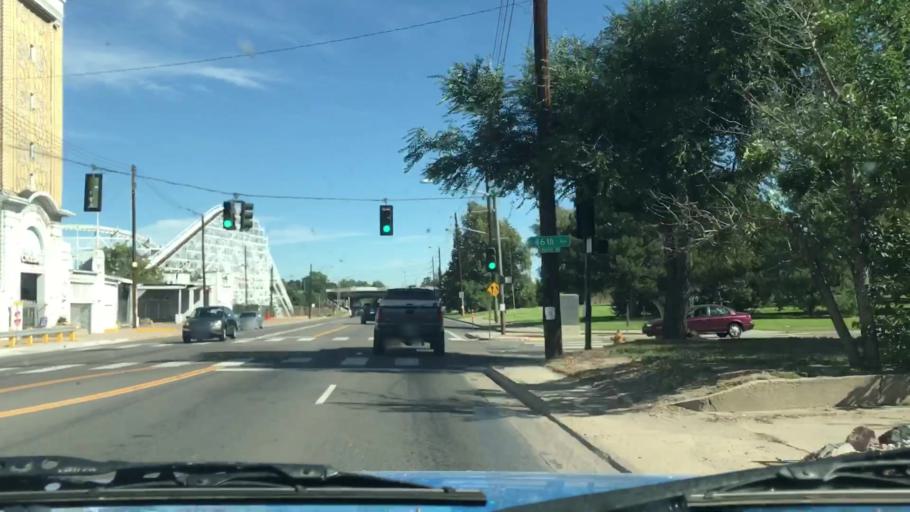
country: US
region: Colorado
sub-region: Jefferson County
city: Wheat Ridge
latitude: 39.7799
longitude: -105.0532
